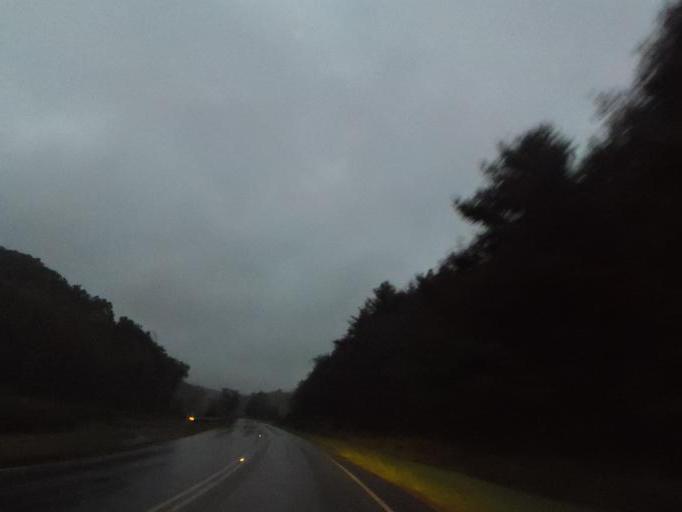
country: US
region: North Carolina
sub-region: Alleghany County
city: Sparta
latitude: 36.5602
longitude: -81.1501
